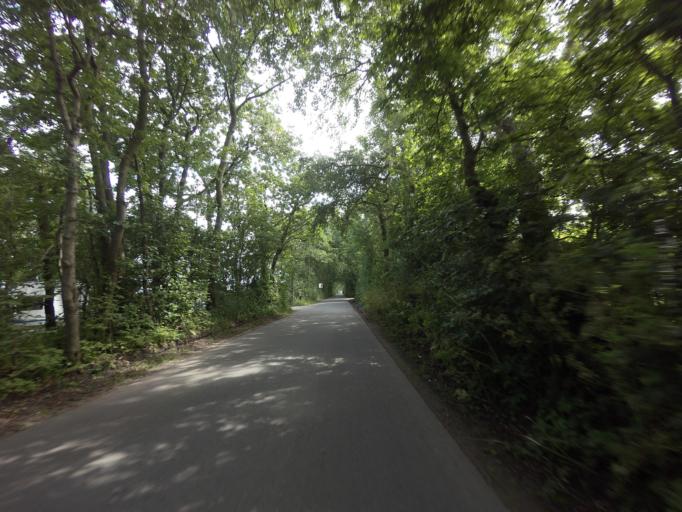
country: NL
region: North Holland
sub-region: Gemeente Schagen
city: Schagen
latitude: 52.8281
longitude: 4.7909
